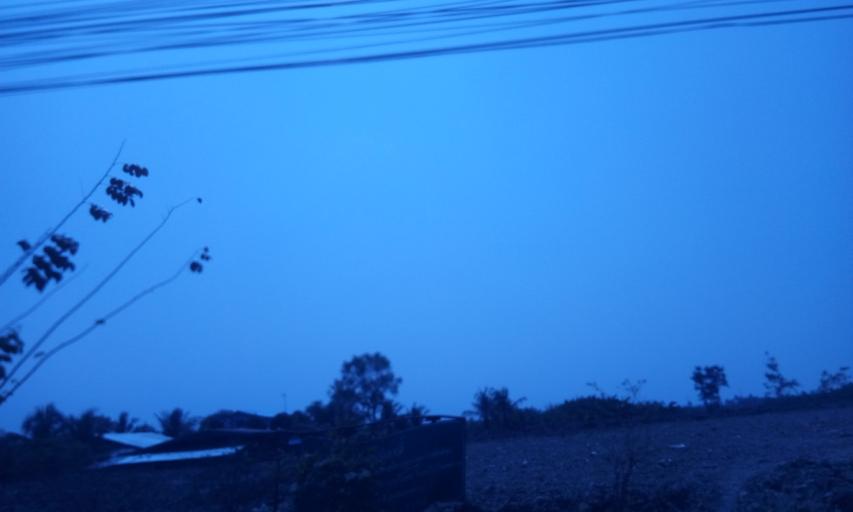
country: TH
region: Nonthaburi
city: Sai Noi
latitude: 13.9110
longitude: 100.3229
